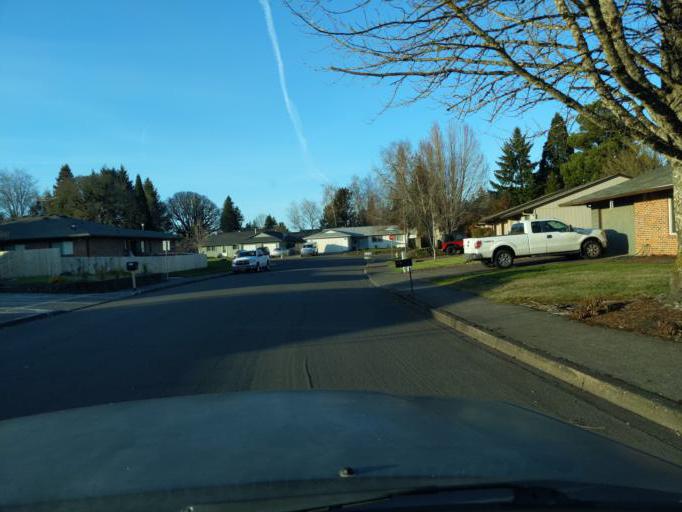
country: US
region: Oregon
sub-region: Yamhill County
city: McMinnville
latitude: 45.2016
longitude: -123.2116
